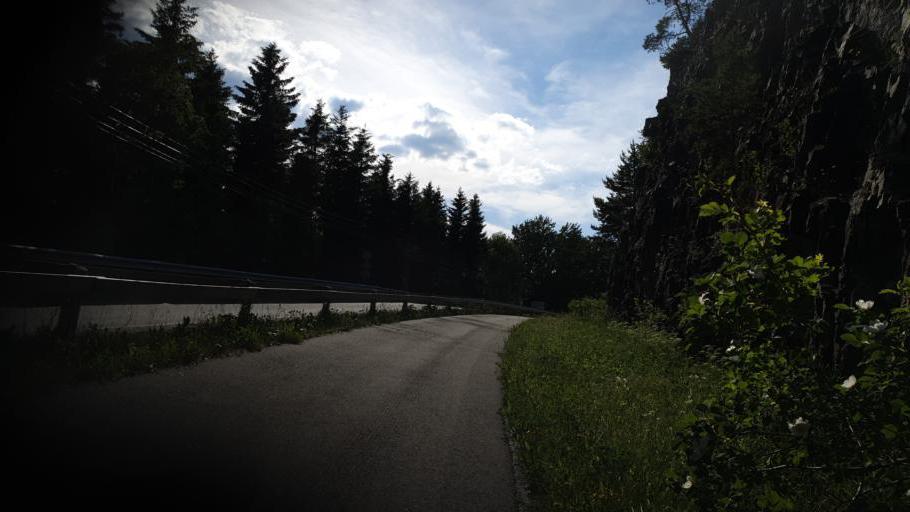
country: NO
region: Sor-Trondelag
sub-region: Trondheim
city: Trondheim
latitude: 63.5695
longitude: 10.4103
